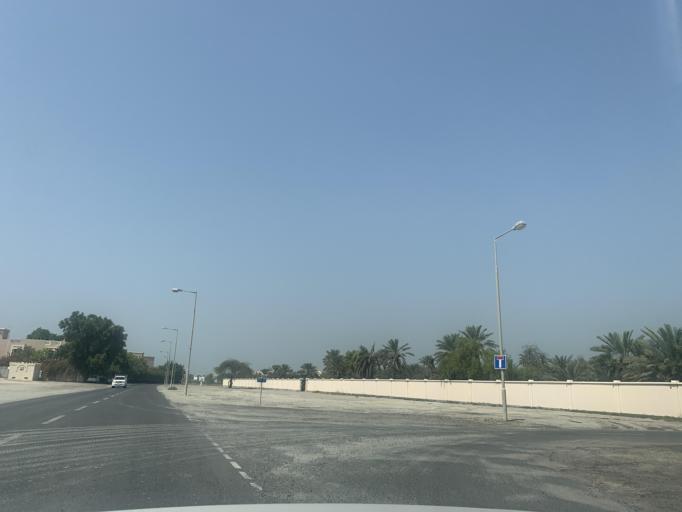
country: BH
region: Central Governorate
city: Madinat Hamad
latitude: 26.1701
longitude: 50.4584
